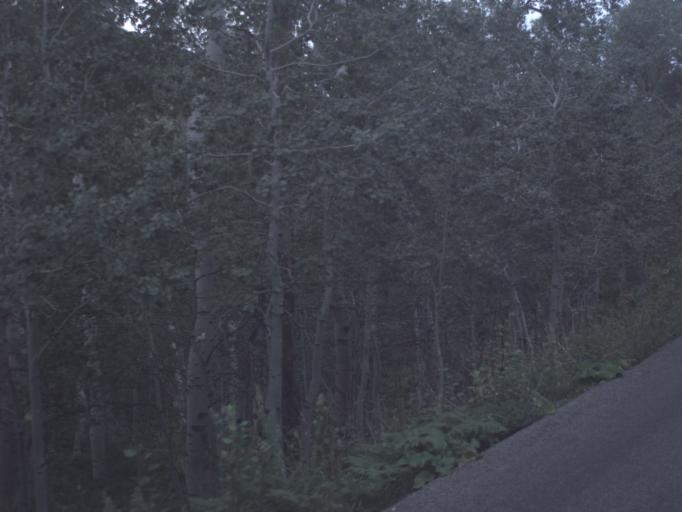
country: US
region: Utah
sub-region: Utah County
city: Lindon
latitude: 40.4251
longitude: -111.6067
